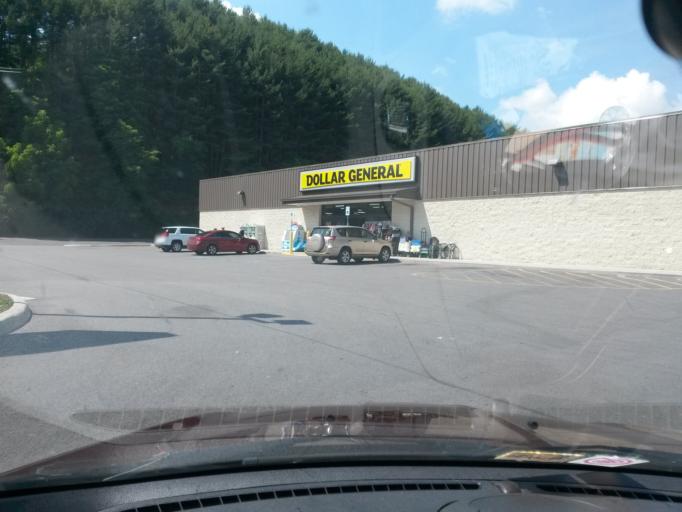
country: US
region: West Virginia
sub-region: Mercer County
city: Princeton
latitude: 37.3833
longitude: -81.1215
